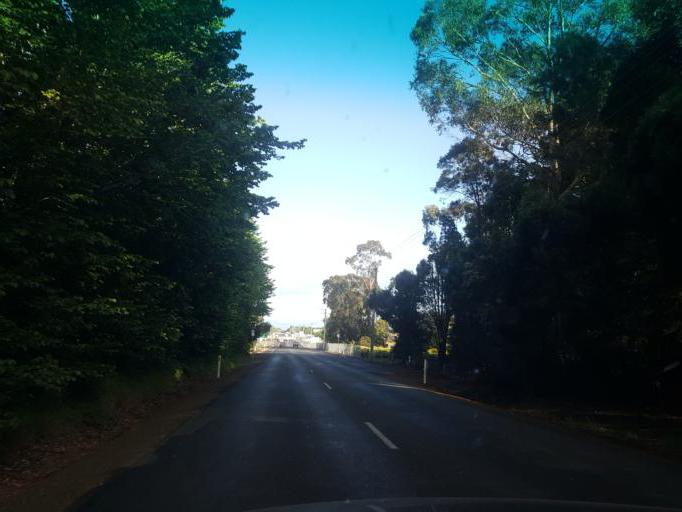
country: AU
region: Tasmania
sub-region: Northern Midlands
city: Perth
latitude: -41.5441
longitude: 147.2041
